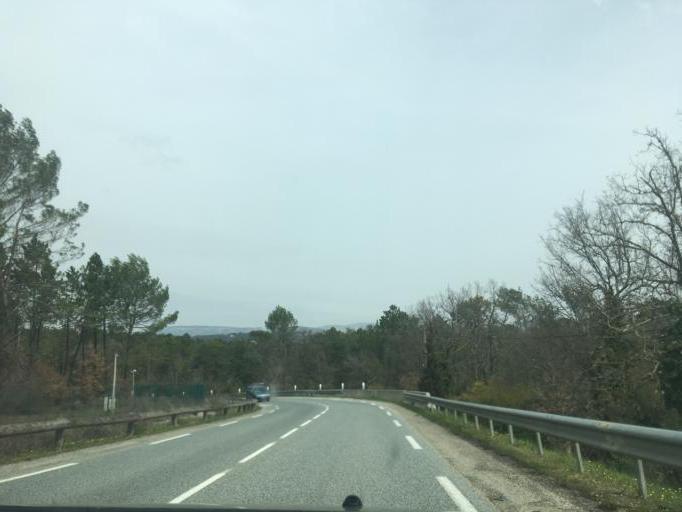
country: FR
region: Provence-Alpes-Cote d'Azur
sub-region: Departement du Var
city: Callian
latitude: 43.5980
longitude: 6.7414
